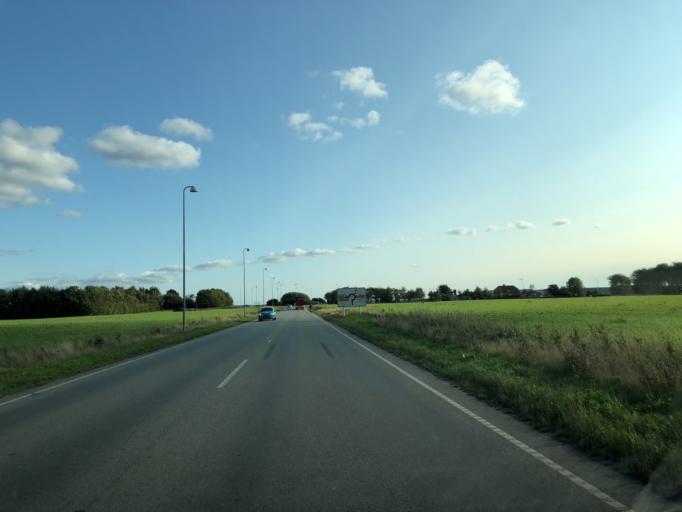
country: DK
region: Central Jutland
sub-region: Viborg Kommune
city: Viborg
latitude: 56.4517
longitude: 9.3431
